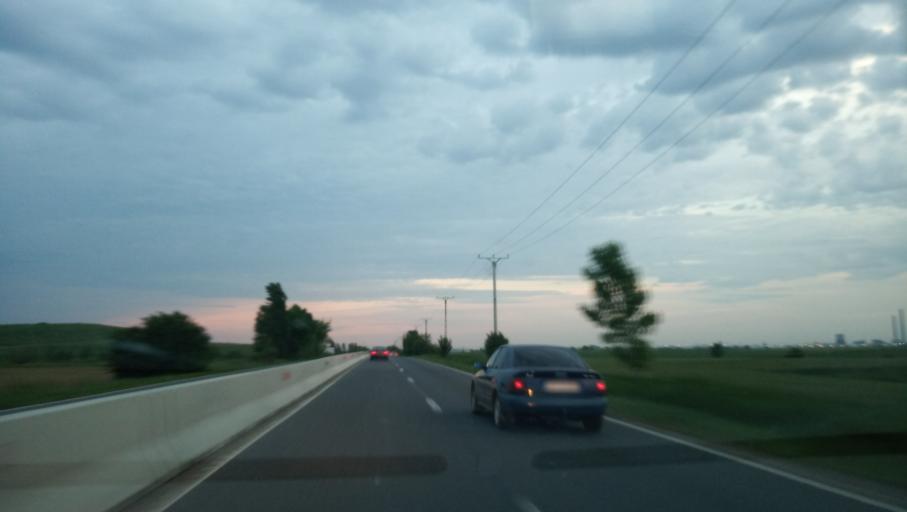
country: RO
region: Timis
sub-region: Comuna Sag
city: Sag
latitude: 45.6740
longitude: 21.1707
